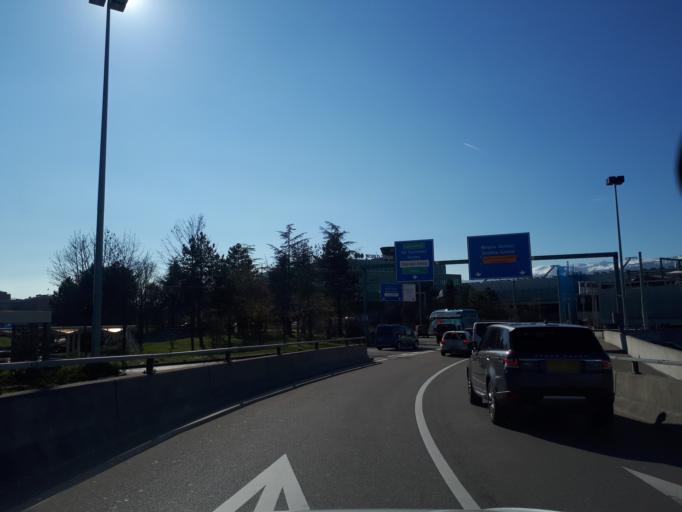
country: CH
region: Geneva
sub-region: Geneva
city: Les Avanchets
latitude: 46.2292
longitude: 6.1078
